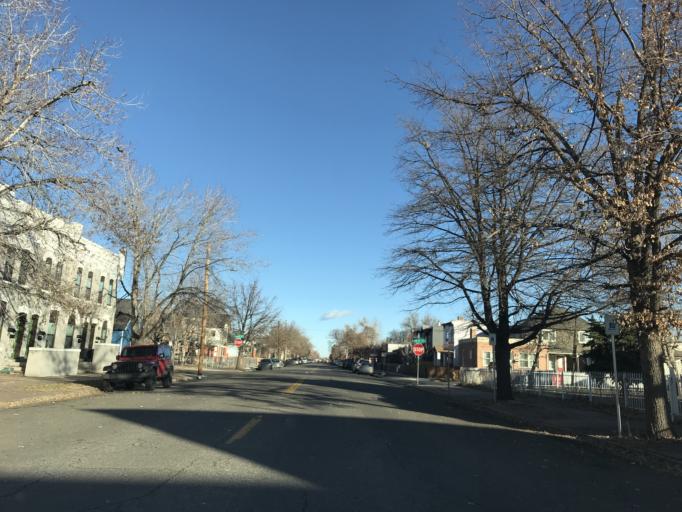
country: US
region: Colorado
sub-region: Denver County
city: Denver
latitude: 39.7663
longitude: -104.9660
